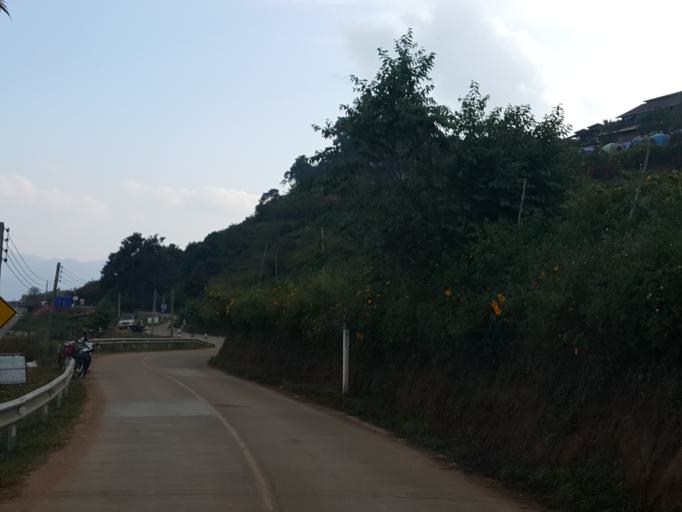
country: TH
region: Chiang Mai
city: Samoeng
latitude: 18.9346
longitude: 98.8153
